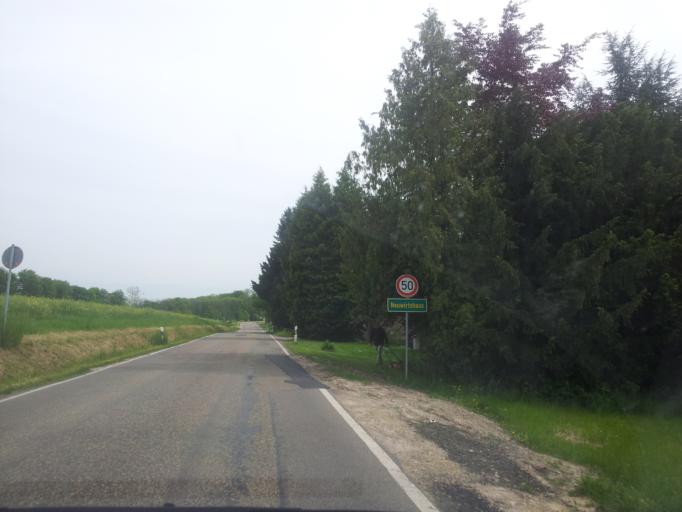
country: DE
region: Baden-Wuerttemberg
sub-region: Regierungsbezirk Stuttgart
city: Oberstenfeld
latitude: 49.0058
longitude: 9.3421
